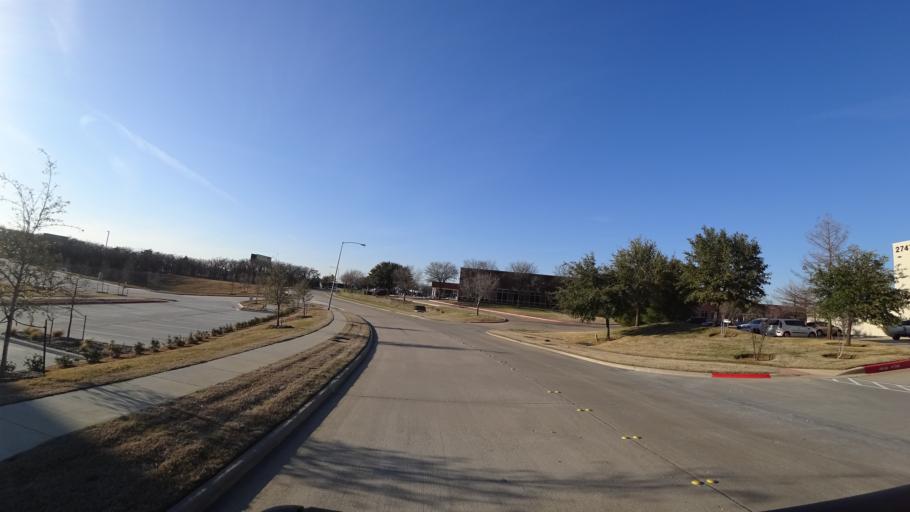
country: US
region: Texas
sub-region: Dallas County
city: Coppell
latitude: 32.9957
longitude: -96.9978
